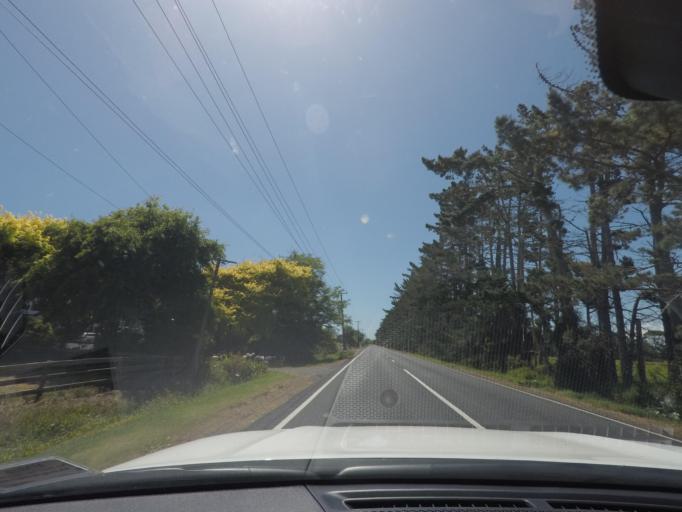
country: NZ
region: Auckland
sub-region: Auckland
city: Parakai
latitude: -36.6555
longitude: 174.4271
